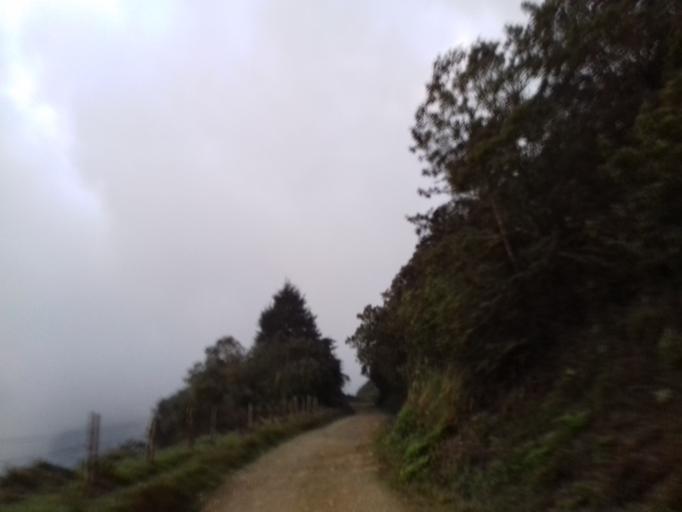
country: CO
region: Quindio
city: Salento
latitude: 4.5601
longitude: -75.5177
